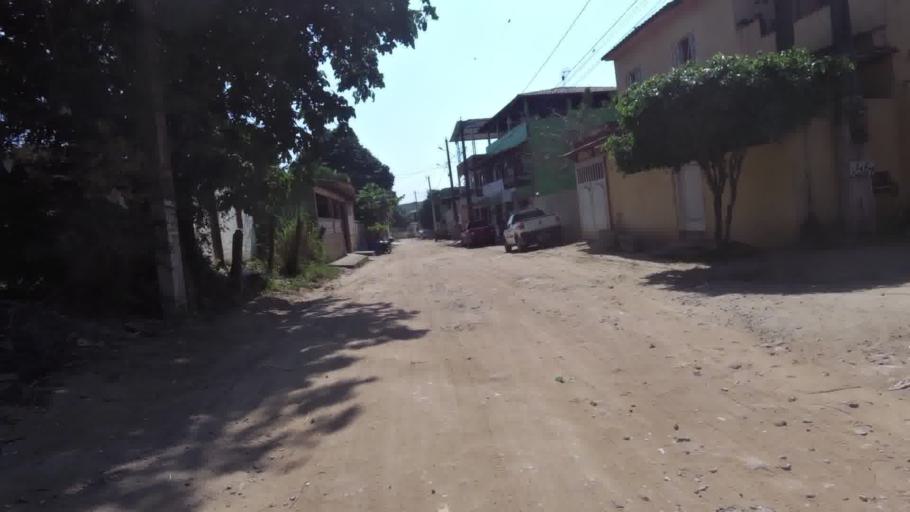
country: BR
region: Espirito Santo
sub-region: Marataizes
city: Marataizes
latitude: -21.0295
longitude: -40.8240
